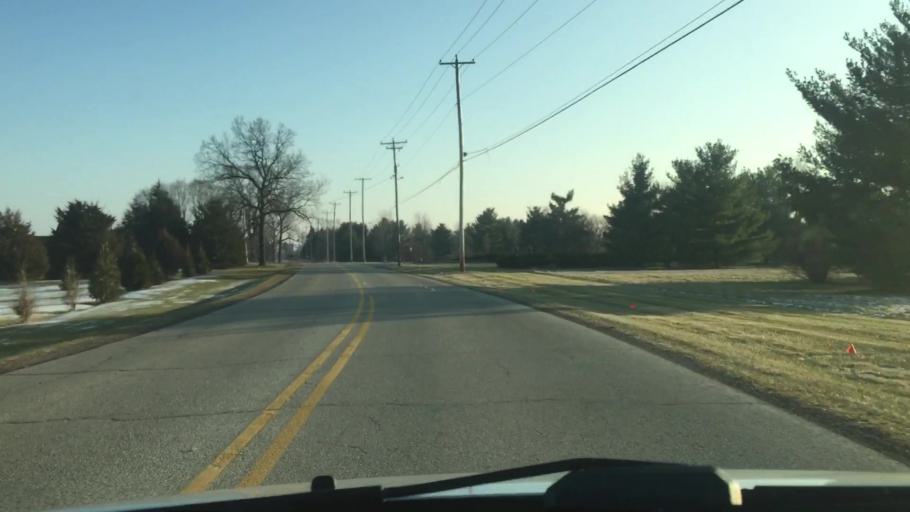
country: US
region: Wisconsin
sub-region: Waukesha County
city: Dousman
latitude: 43.0435
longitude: -88.4870
